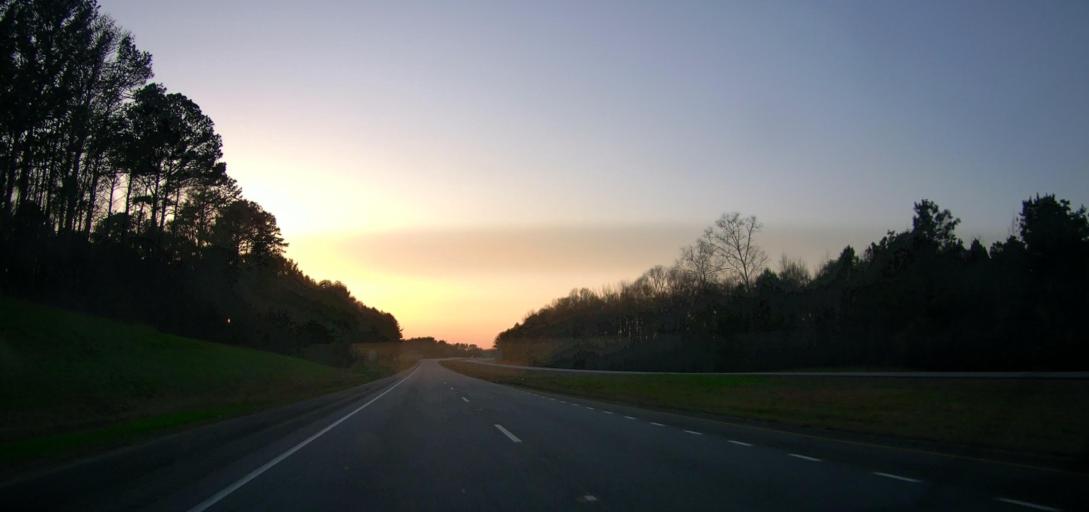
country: US
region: Alabama
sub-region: Coosa County
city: Goodwater
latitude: 32.9802
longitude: -86.0549
